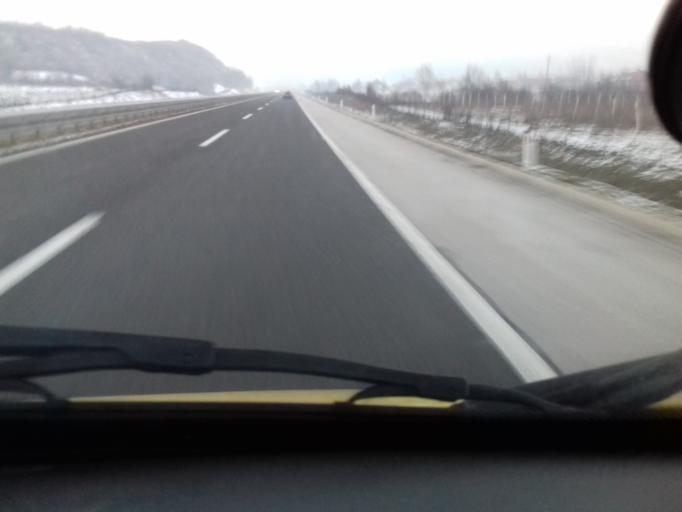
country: BA
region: Federation of Bosnia and Herzegovina
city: Mahala
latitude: 43.9803
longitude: 18.2344
